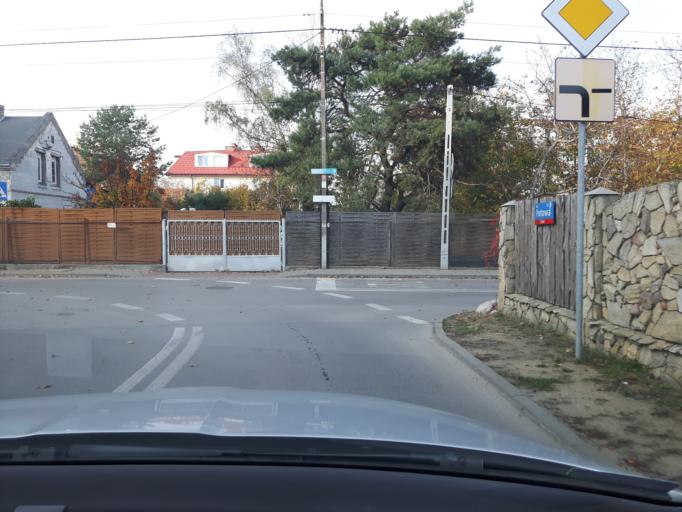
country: PL
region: Masovian Voivodeship
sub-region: Warszawa
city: Bialoleka
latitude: 52.3075
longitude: 20.9778
